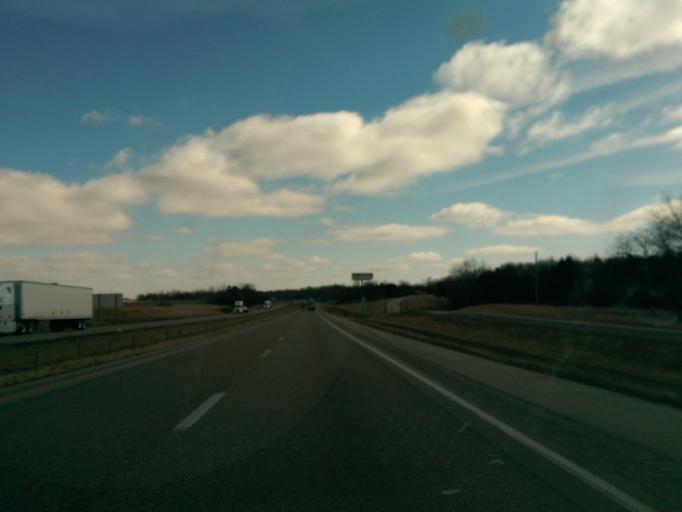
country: US
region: Missouri
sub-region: Montgomery County
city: Montgomery City
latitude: 38.8699
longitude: -91.3632
